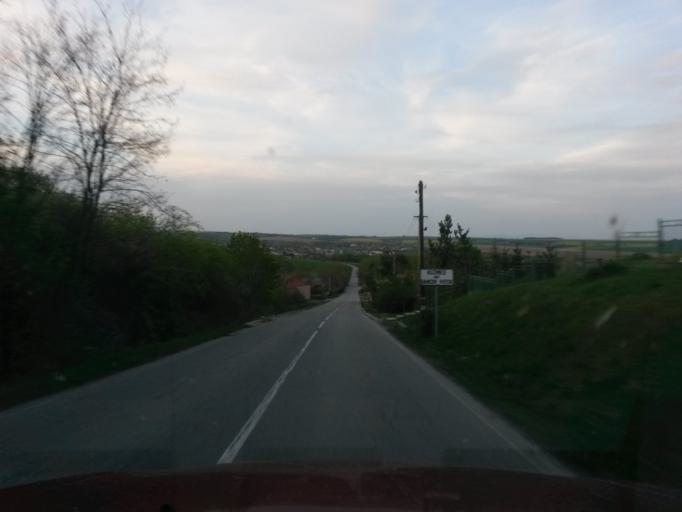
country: SK
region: Kosicky
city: Secovce
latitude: 48.5602
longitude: 21.5601
